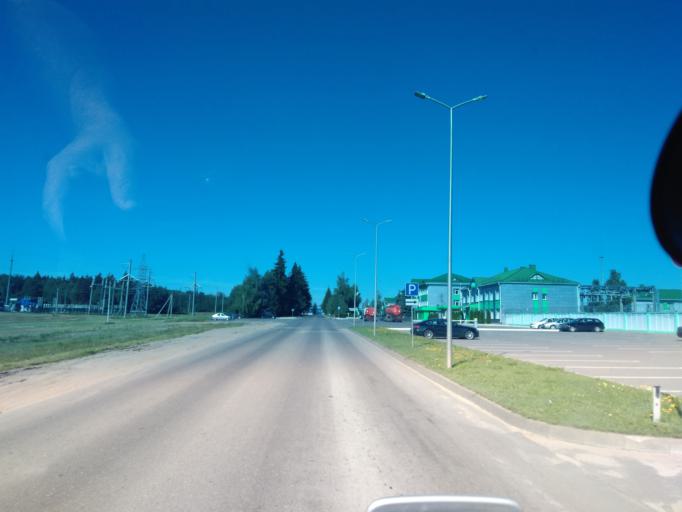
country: BY
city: Fanipol
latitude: 53.7409
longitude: 27.3511
